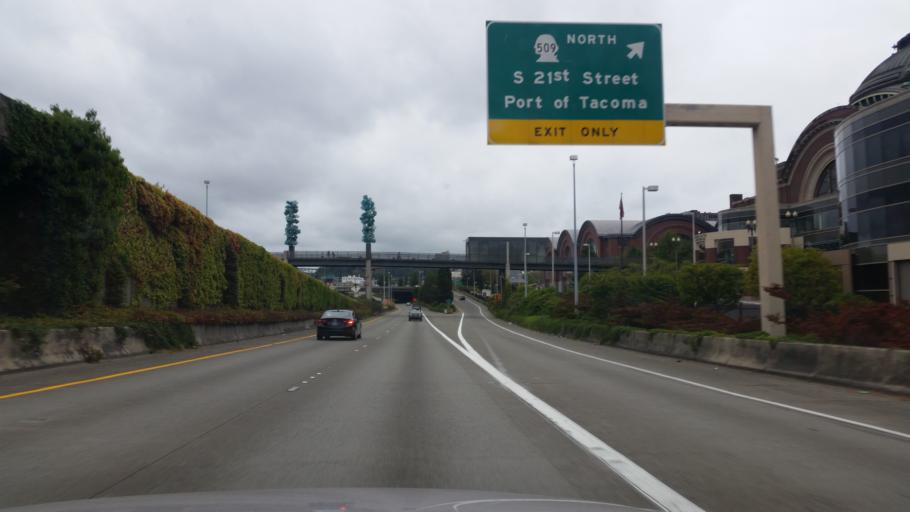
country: US
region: Washington
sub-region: Pierce County
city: Tacoma
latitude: 47.2468
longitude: -122.4356
